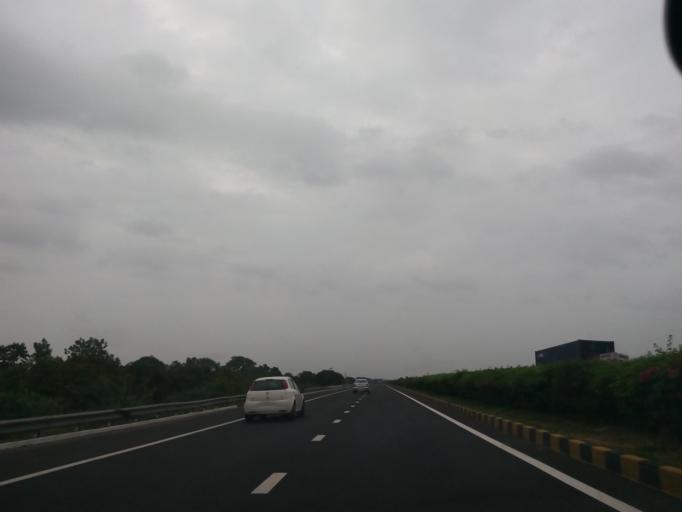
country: IN
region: Gujarat
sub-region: Kheda
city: Nadiad
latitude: 22.7144
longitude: 72.8838
